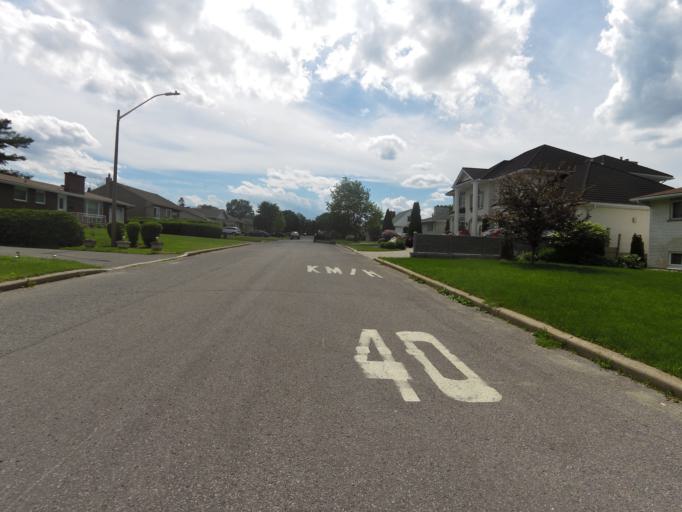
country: CA
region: Ontario
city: Ottawa
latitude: 45.3683
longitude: -75.7178
